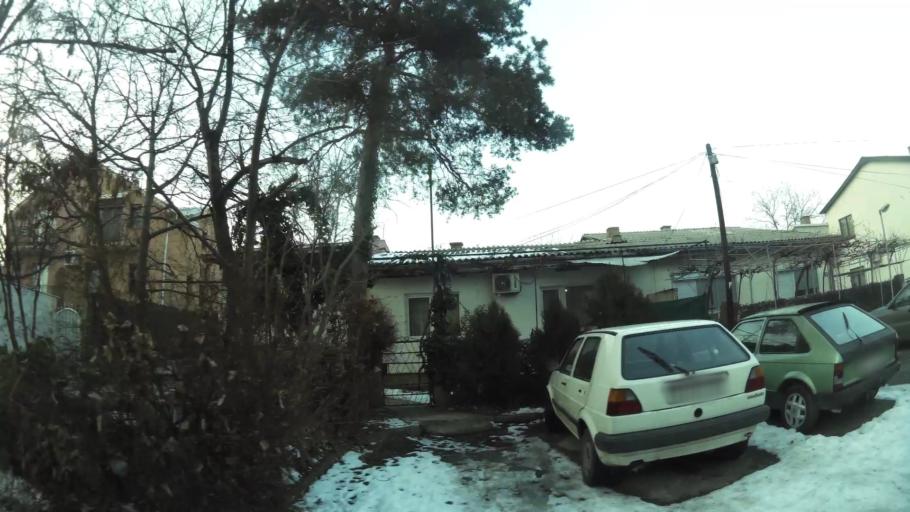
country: MK
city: Creshevo
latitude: 42.0079
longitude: 21.5083
